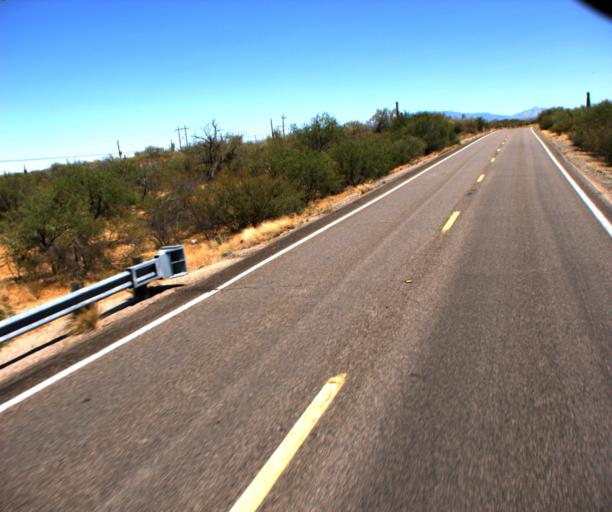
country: US
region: Arizona
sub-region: Pima County
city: Catalina
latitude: 32.7221
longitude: -111.1087
